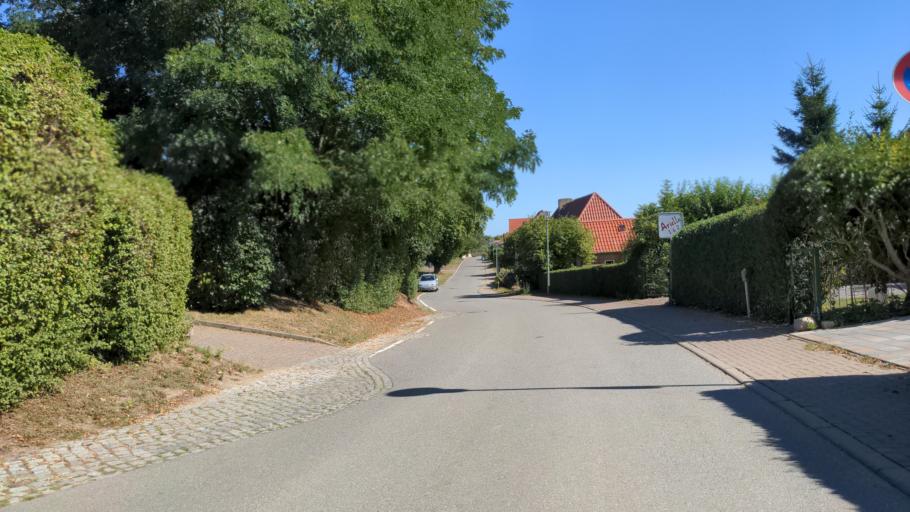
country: DE
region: Mecklenburg-Vorpommern
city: Ostseebad Boltenhagen
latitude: 53.9913
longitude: 11.1807
